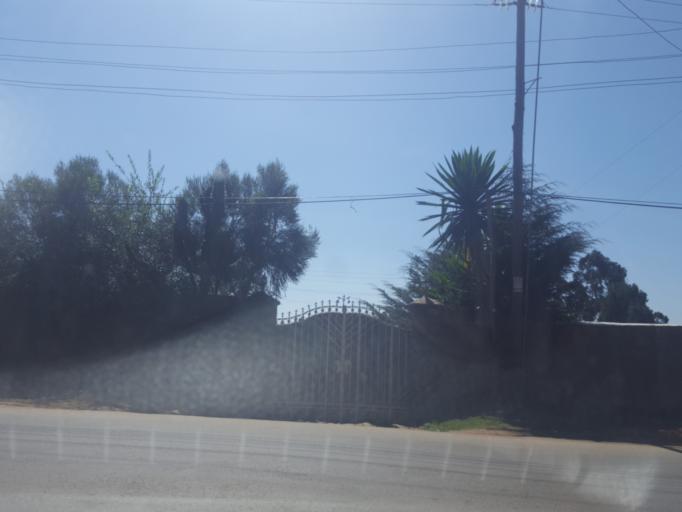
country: ET
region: Adis Abeba
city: Addis Ababa
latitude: 9.0629
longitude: 38.7433
